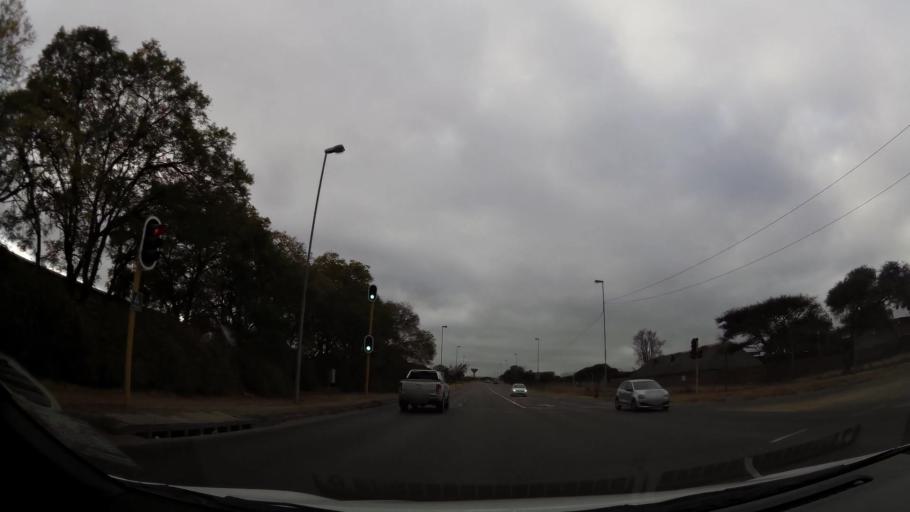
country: ZA
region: Limpopo
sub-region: Capricorn District Municipality
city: Polokwane
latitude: -23.8727
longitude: 29.4553
